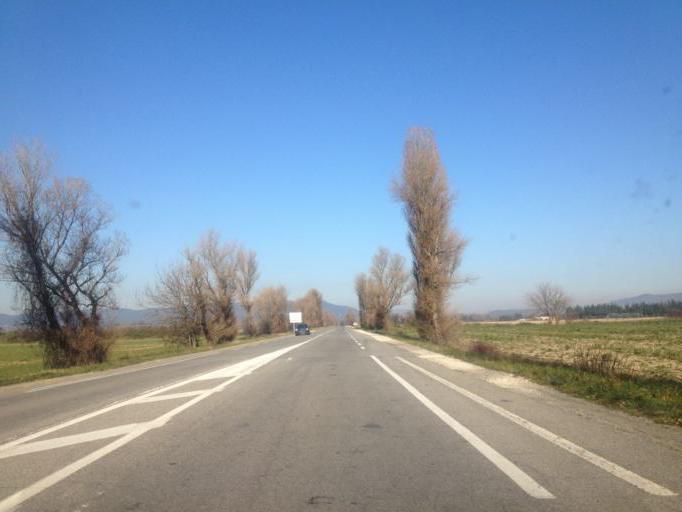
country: FR
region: Rhone-Alpes
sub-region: Departement de la Drome
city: Pierrelatte
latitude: 44.3975
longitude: 4.7021
